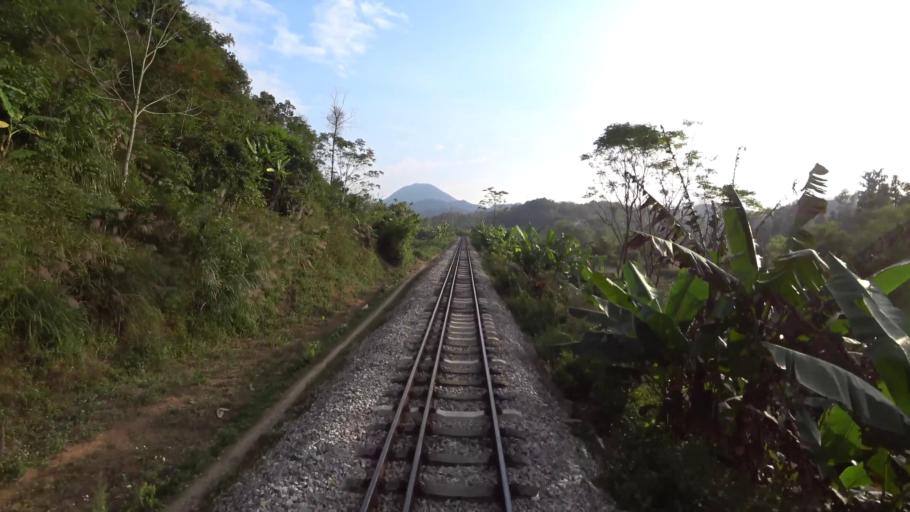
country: VN
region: Lang Son
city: Thi Tran Cao Loc
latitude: 21.9227
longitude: 106.7073
